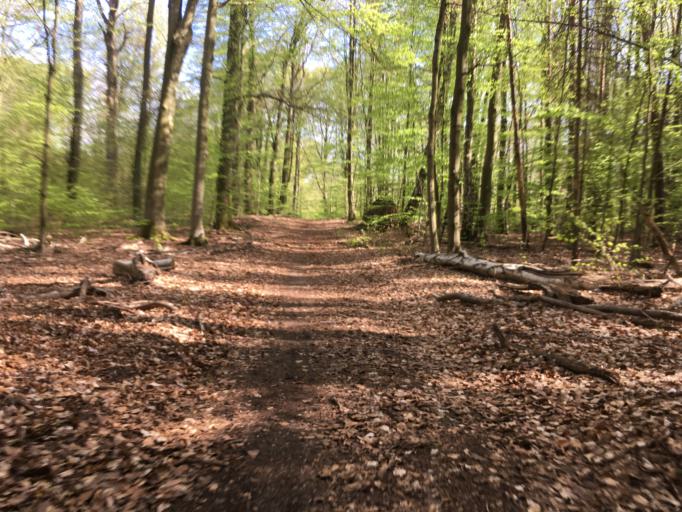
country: DE
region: Brandenburg
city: Bernau bei Berlin
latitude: 52.7339
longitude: 13.5635
